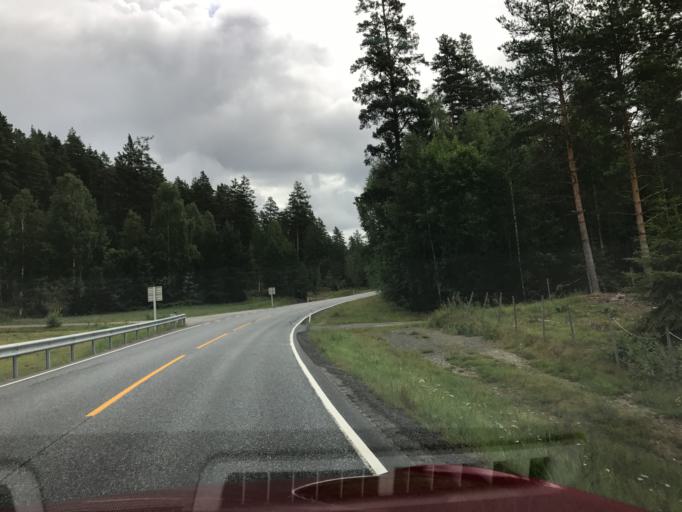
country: NO
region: Buskerud
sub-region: Flesberg
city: Lampeland
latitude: 59.8411
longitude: 9.5498
